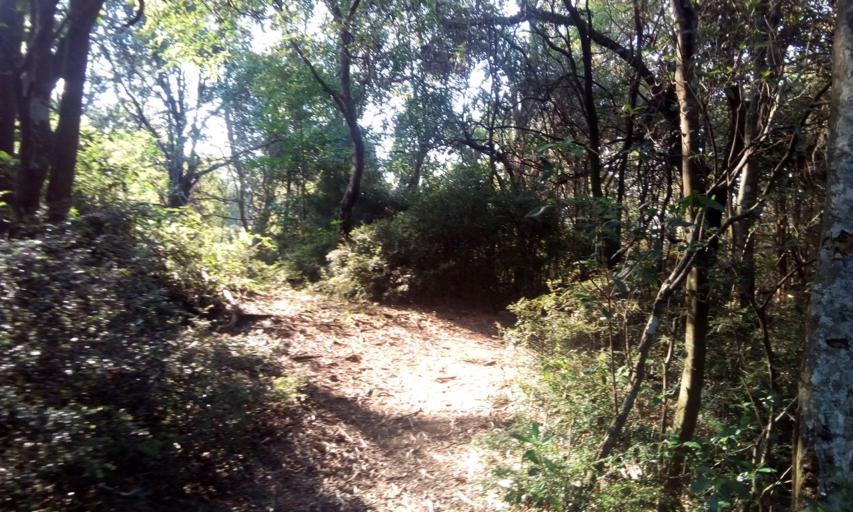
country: AU
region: New South Wales
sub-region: Wollongong
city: Mount Ousley
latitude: -34.4015
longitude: 150.8634
